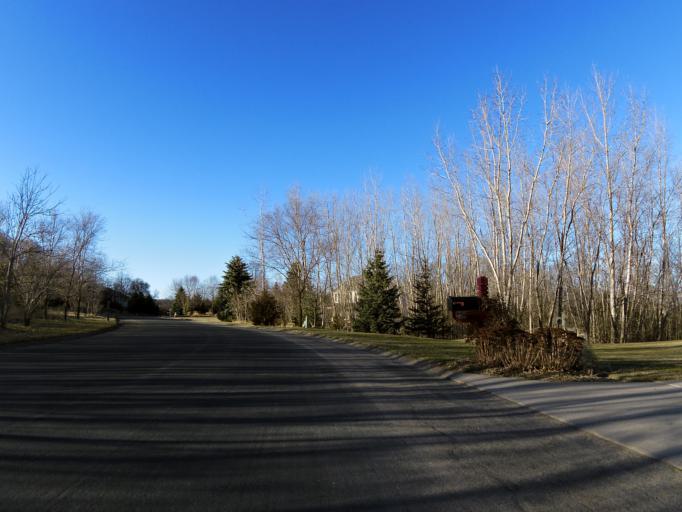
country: US
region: Minnesota
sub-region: Washington County
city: Lakeland
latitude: 44.9687
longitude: -92.8076
